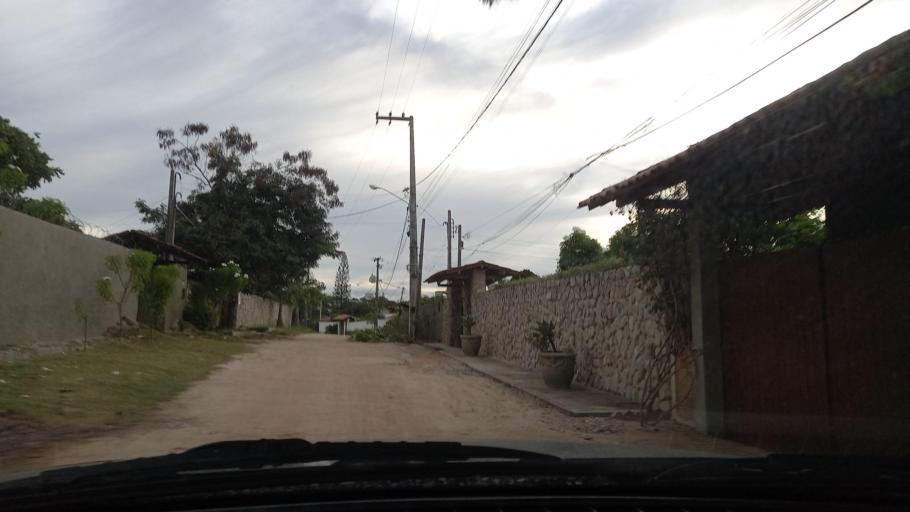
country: BR
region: Pernambuco
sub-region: Gravata
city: Gravata
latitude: -8.1955
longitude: -35.5836
